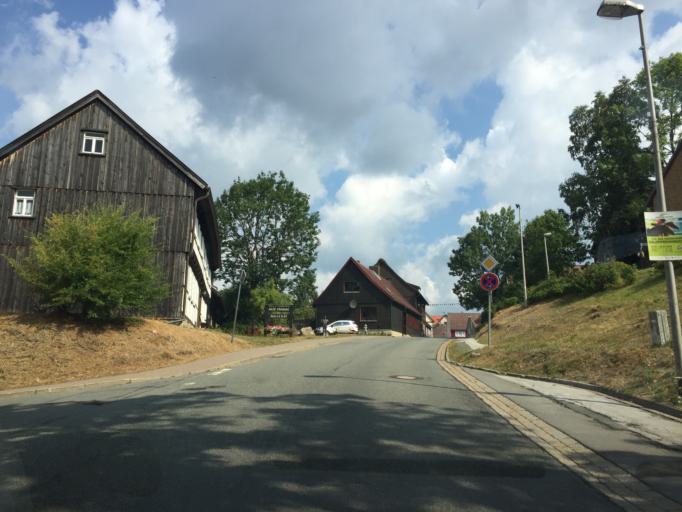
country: DE
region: Lower Saxony
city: Zorge
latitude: 51.6617
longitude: 10.6678
